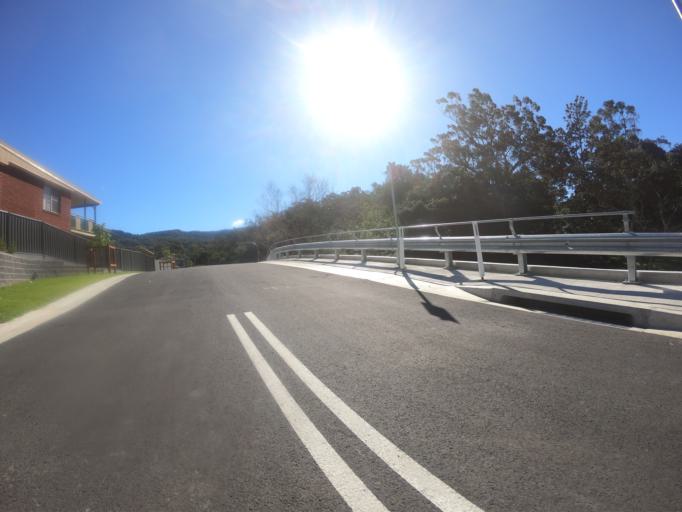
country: AU
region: New South Wales
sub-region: Wollongong
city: Mount Keira
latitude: -34.4300
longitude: 150.8511
